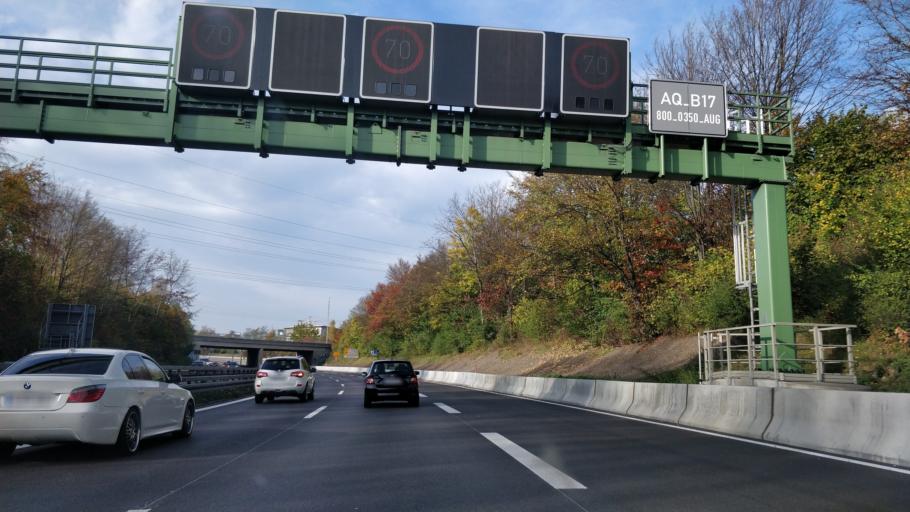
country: DE
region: Bavaria
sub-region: Swabia
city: Augsburg
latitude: 48.3409
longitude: 10.8895
